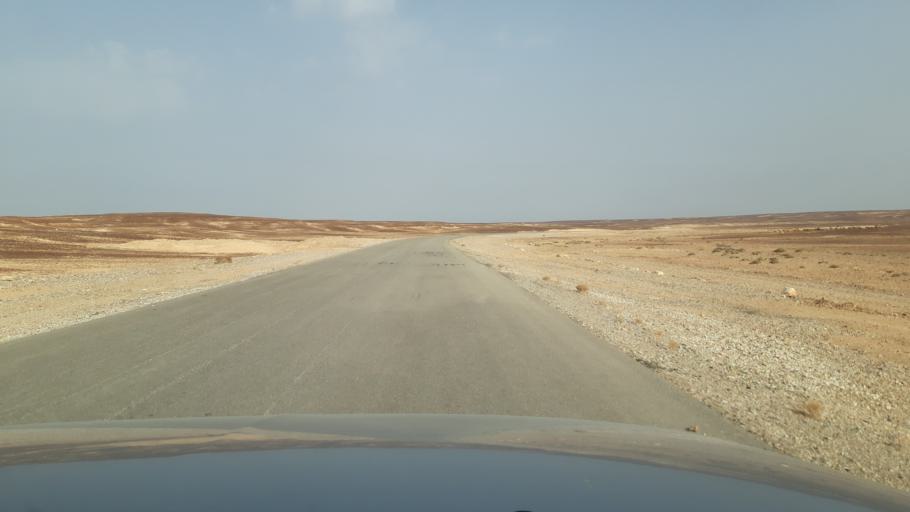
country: JO
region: Amman
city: Al Azraq ash Shamali
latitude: 31.2770
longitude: 36.5849
